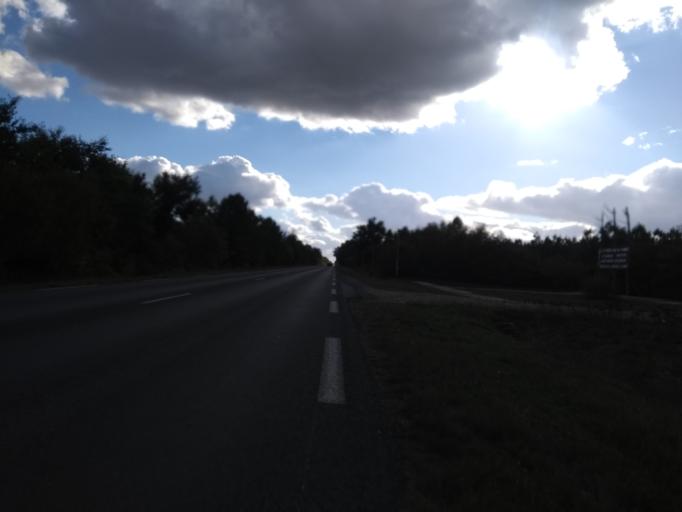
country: FR
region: Aquitaine
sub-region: Departement de la Gironde
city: Saint-Aubin-de-Medoc
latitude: 44.6770
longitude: -0.7274
